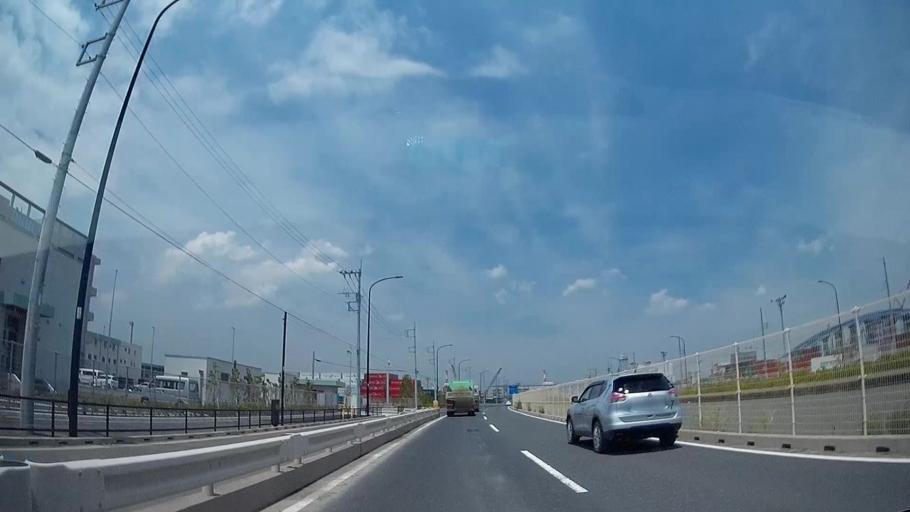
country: JP
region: Kanagawa
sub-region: Kawasaki-shi
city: Kawasaki
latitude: 35.5930
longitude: 139.8020
